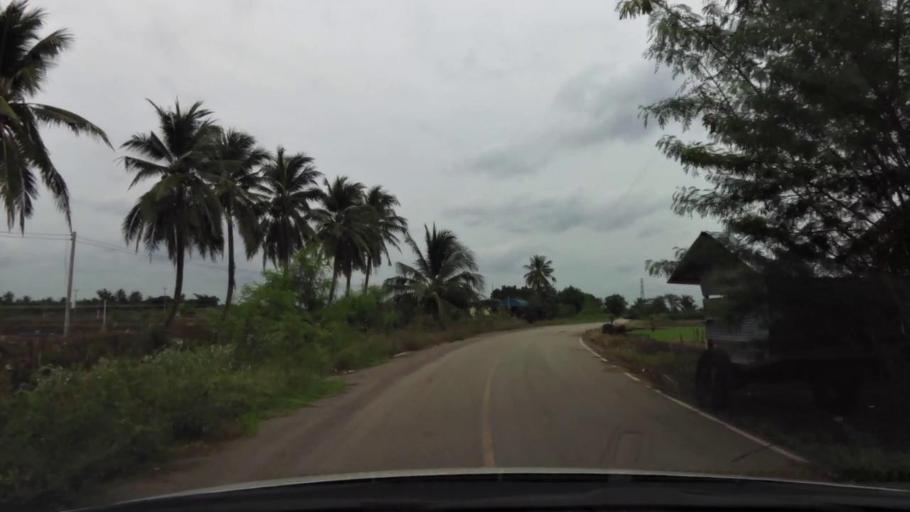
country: TH
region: Samut Sakhon
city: Ban Phaeo
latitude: 13.6134
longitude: 100.0309
